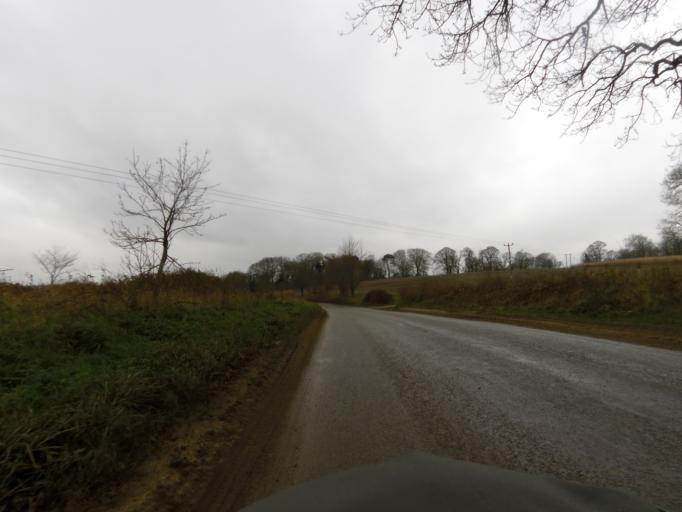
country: GB
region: England
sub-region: Norfolk
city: Briston
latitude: 52.8800
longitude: 1.0782
